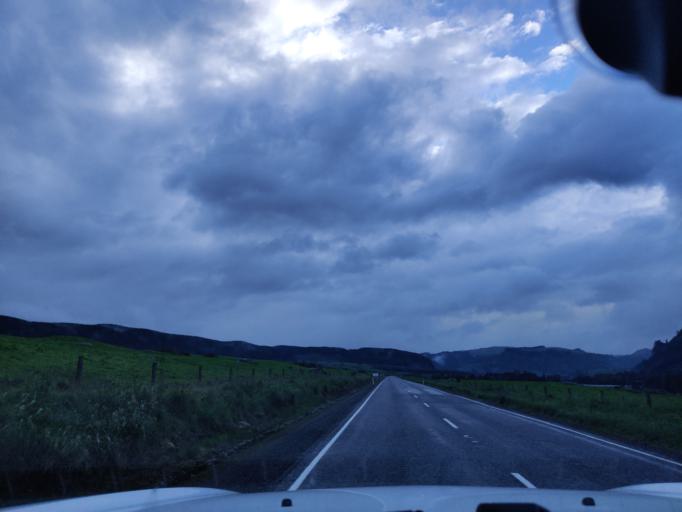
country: NZ
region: Waikato
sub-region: South Waikato District
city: Tokoroa
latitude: -38.4101
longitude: 175.7997
